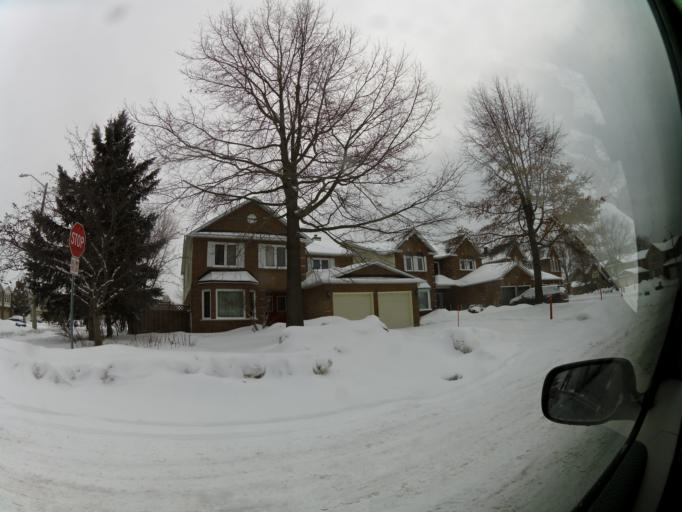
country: CA
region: Ontario
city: Ottawa
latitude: 45.3760
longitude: -75.6150
